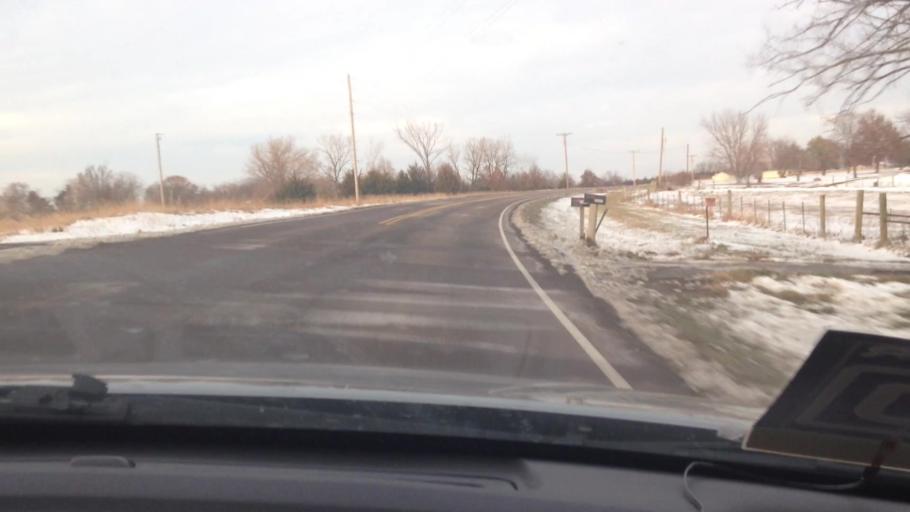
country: US
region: Kansas
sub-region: Leavenworth County
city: Lansing
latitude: 39.2324
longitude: -94.9843
